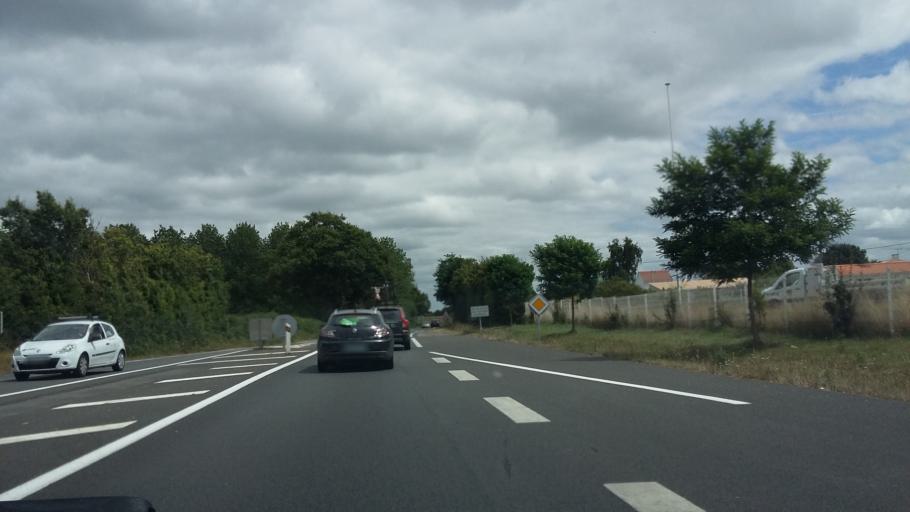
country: FR
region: Pays de la Loire
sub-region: Departement de la Vendee
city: Challans
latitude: 46.8371
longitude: -1.8431
